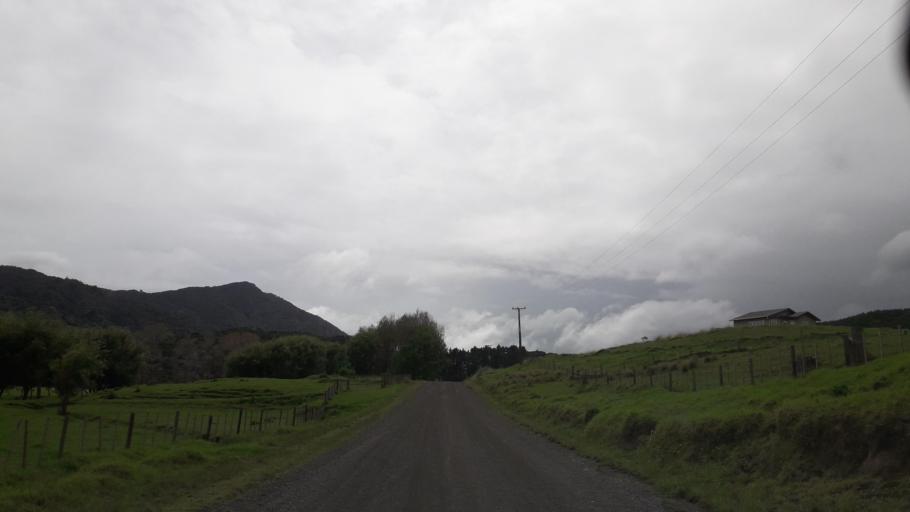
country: NZ
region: Northland
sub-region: Far North District
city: Ahipara
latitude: -35.4398
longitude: 173.3268
